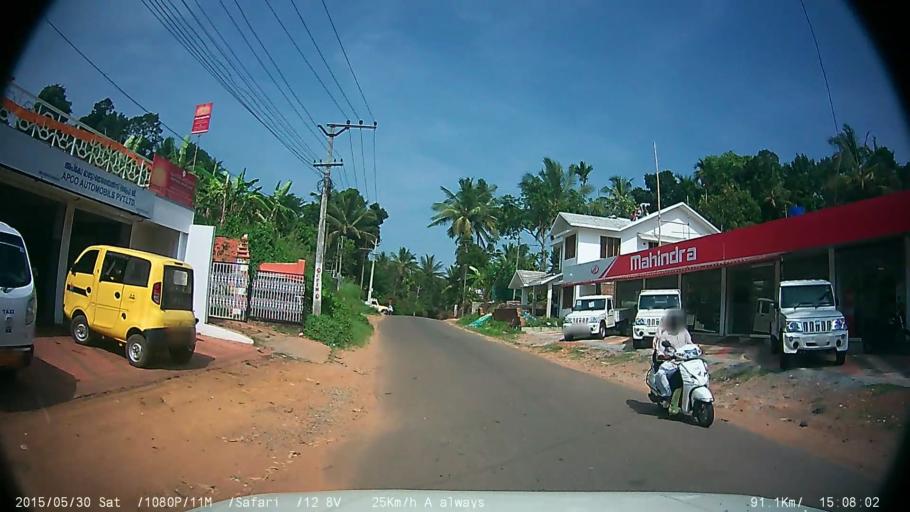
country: IN
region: Kerala
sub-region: Wayanad
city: Panamaram
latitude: 11.8005
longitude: 76.0186
